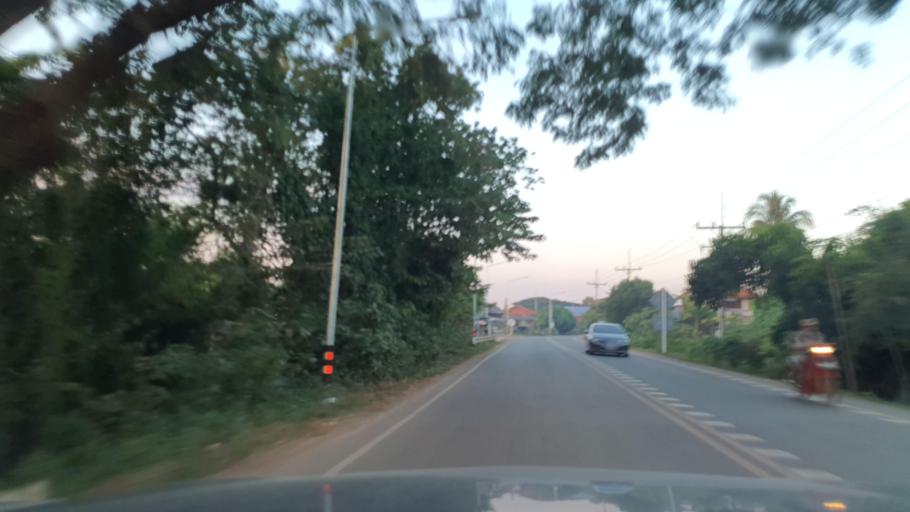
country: TH
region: Phayao
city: Dok Kham Tai
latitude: 19.0257
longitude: 100.0625
